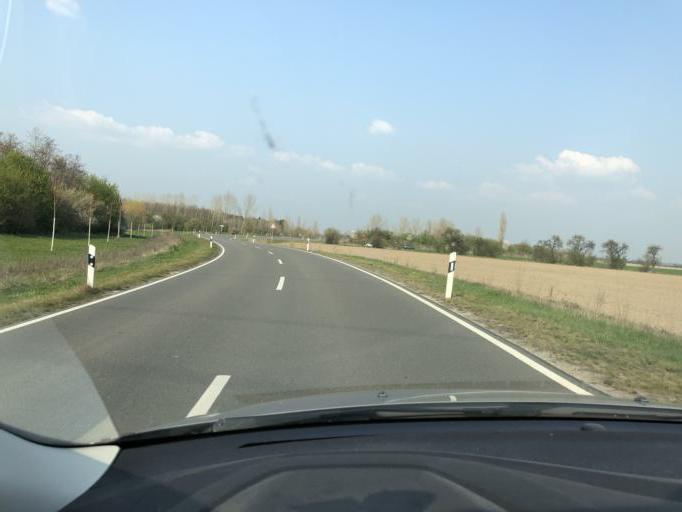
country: DE
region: Saxony
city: Zwochau
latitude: 51.4219
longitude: 12.3150
